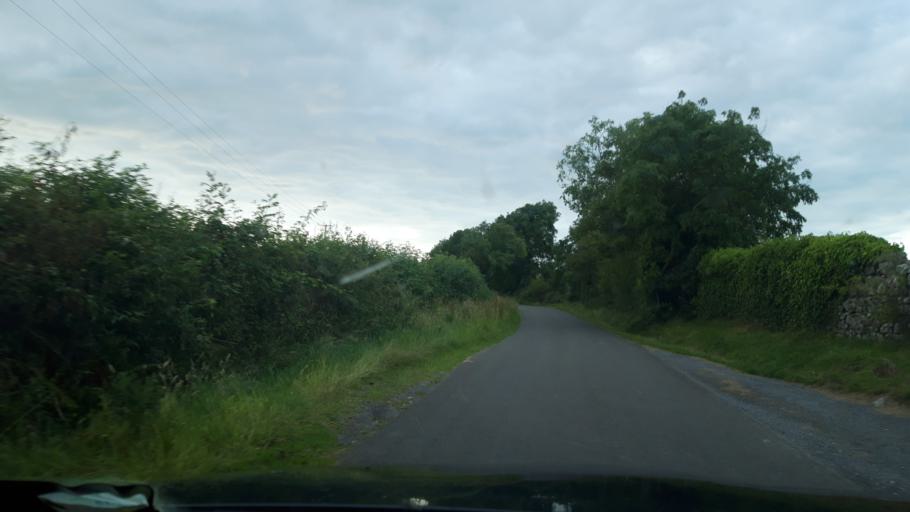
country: IE
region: Leinster
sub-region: Kilkenny
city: Graiguenamanagh
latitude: 52.5839
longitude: -6.9923
